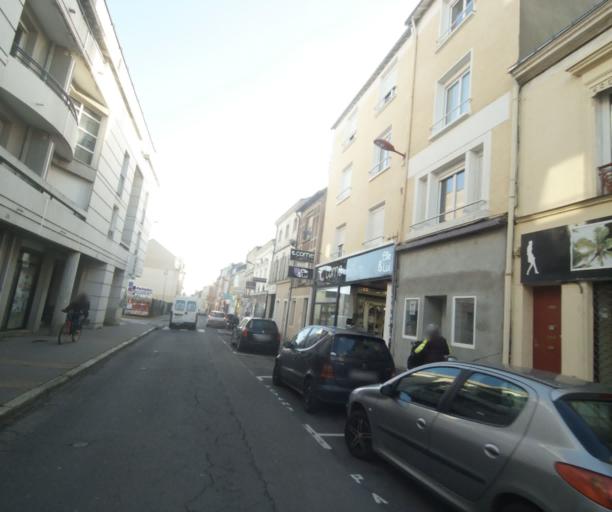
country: FR
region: Pays de la Loire
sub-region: Departement de la Sarthe
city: Le Mans
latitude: 47.9985
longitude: 0.2003
